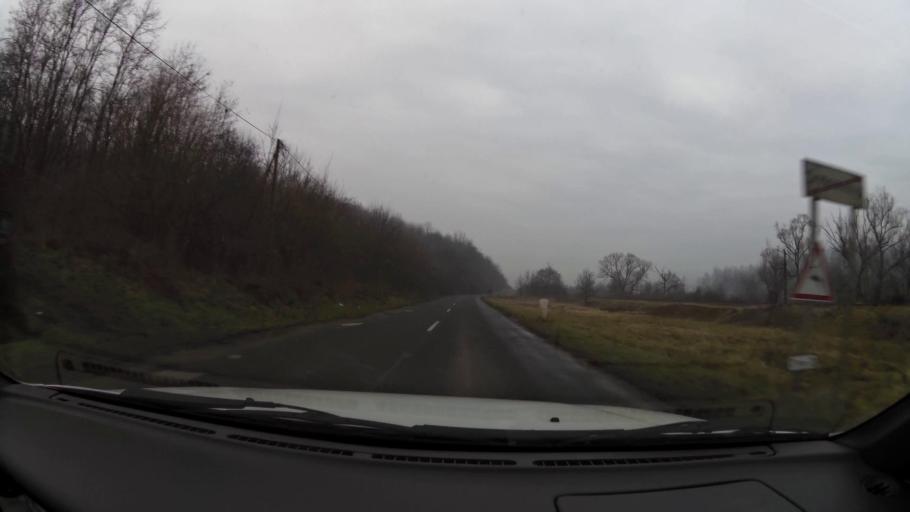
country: HU
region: Borsod-Abauj-Zemplen
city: Rudabanya
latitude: 48.3420
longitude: 20.6446
